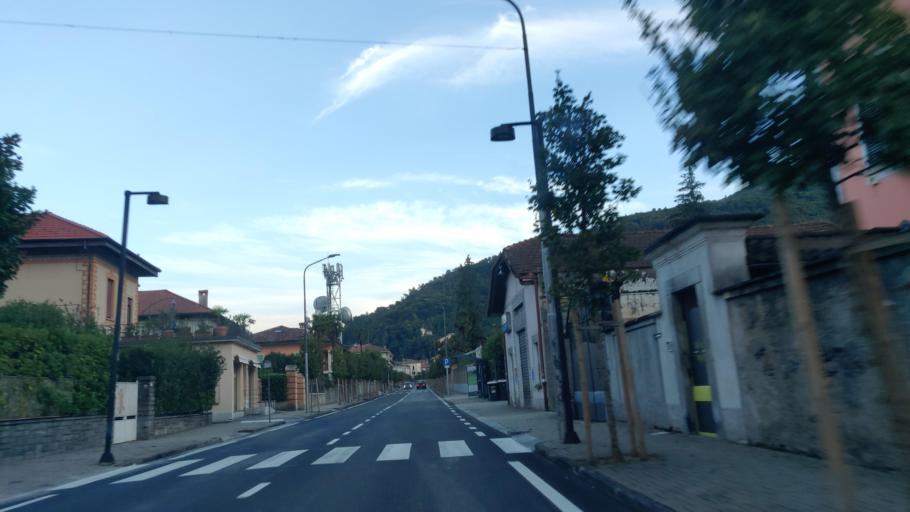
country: IT
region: Piedmont
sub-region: Provincia Verbano-Cusio-Ossola
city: Cannobio
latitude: 46.0658
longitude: 8.6961
